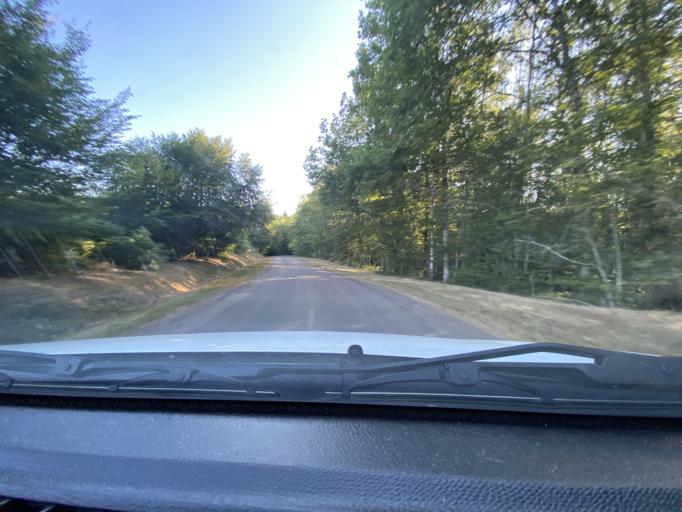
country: FR
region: Bourgogne
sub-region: Departement de la Cote-d'Or
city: Saulieu
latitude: 47.3038
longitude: 4.1788
